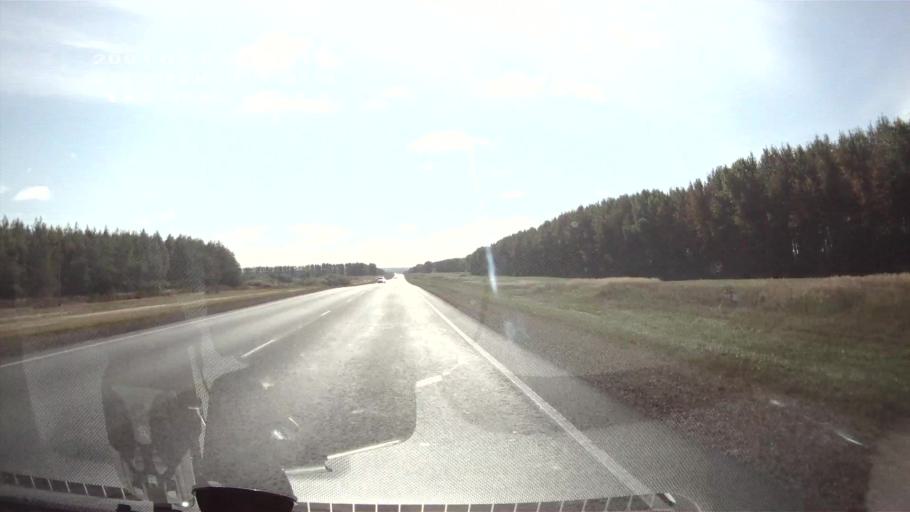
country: RU
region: Ulyanovsk
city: Tsil'na
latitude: 54.5579
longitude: 47.9304
